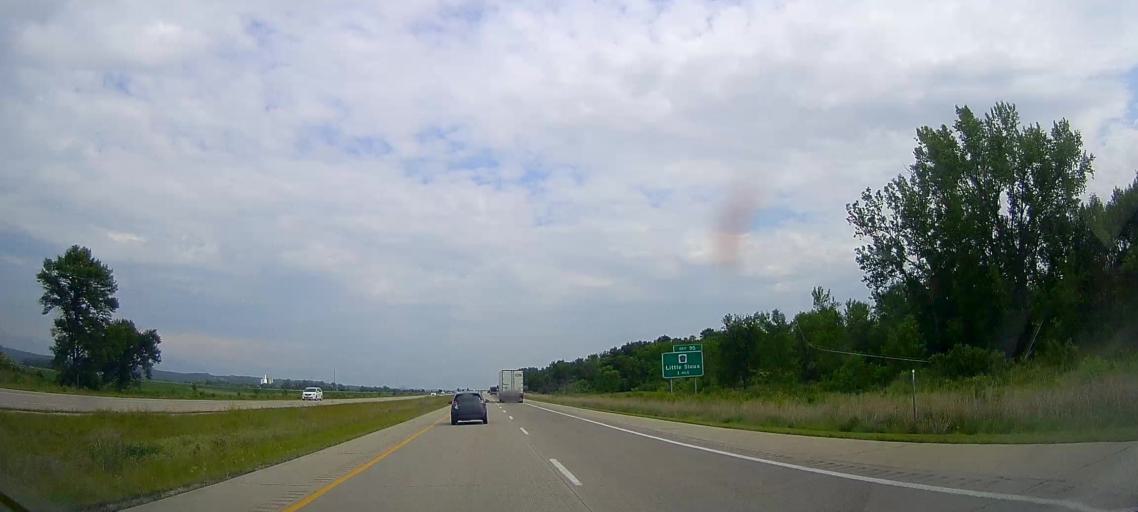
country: US
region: Nebraska
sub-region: Burt County
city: Tekamah
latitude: 41.8165
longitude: -96.0687
